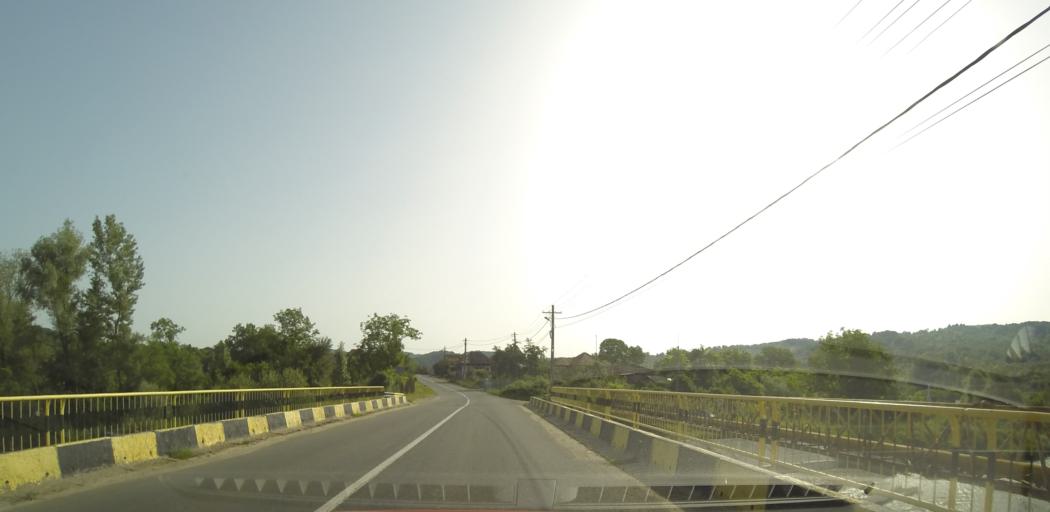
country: RO
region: Valcea
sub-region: Comuna Pausesti-Maglasi
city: Pausesti-Maglasi
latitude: 45.1580
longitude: 24.2484
